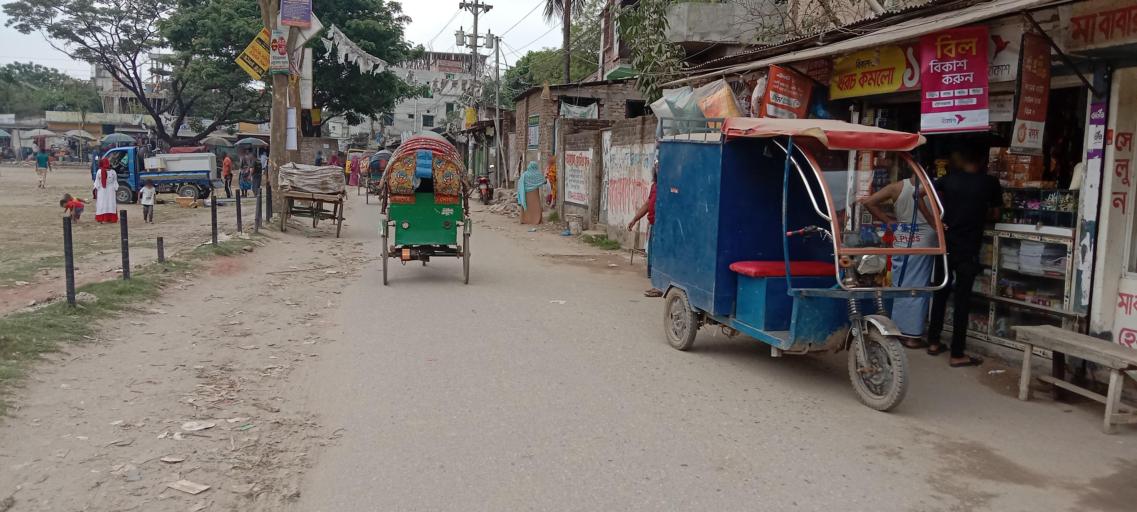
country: BD
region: Dhaka
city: Azimpur
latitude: 23.7361
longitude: 90.3349
